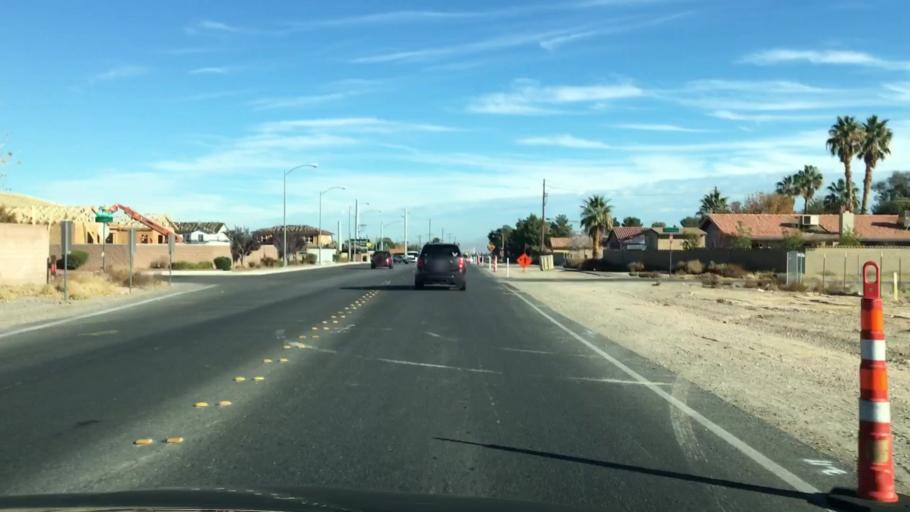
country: US
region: Nevada
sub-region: Clark County
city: Enterprise
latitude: 36.0572
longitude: -115.1931
